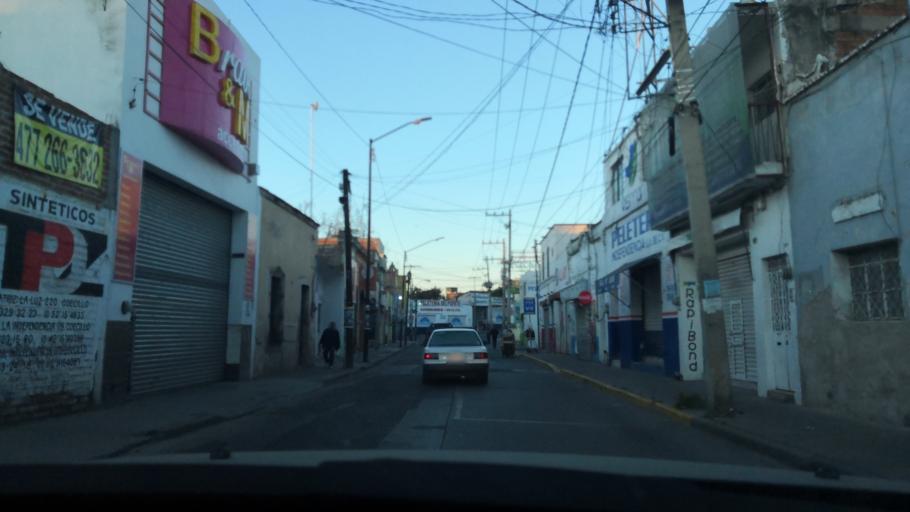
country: MX
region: Guanajuato
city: Leon
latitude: 21.1248
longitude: -101.6723
